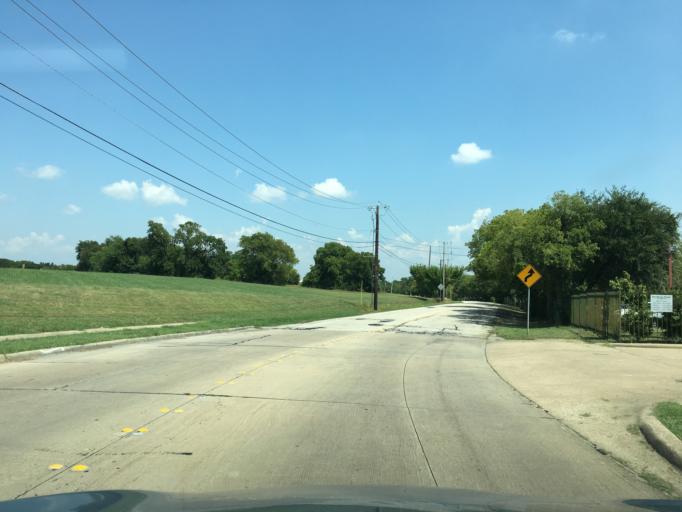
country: US
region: Texas
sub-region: Dallas County
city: Garland
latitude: 32.9500
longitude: -96.6511
